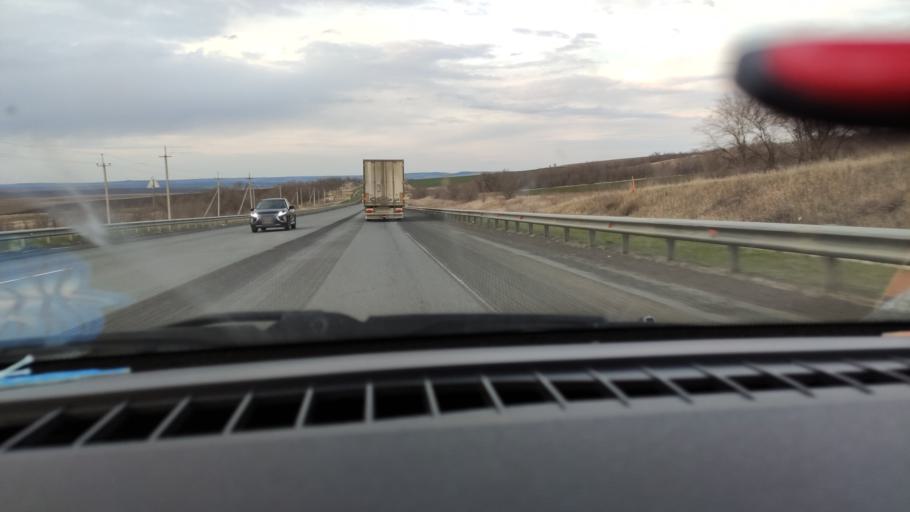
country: RU
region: Saratov
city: Shumeyka
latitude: 51.7836
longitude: 46.1316
